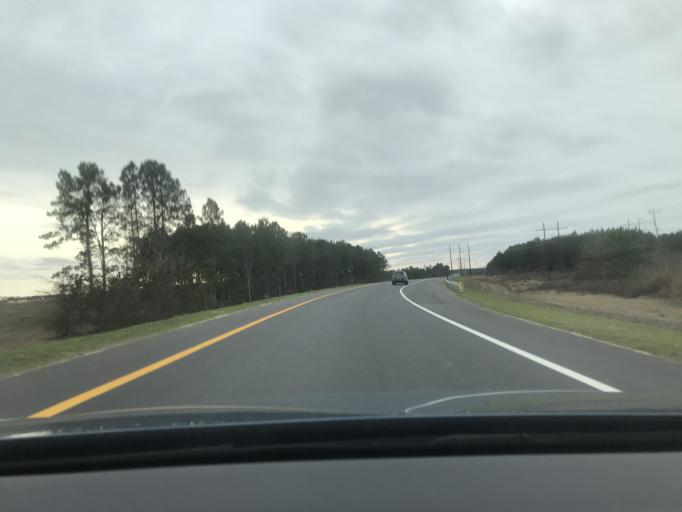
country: US
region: North Carolina
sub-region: Cumberland County
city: Fort Bragg
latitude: 35.0675
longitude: -79.0239
